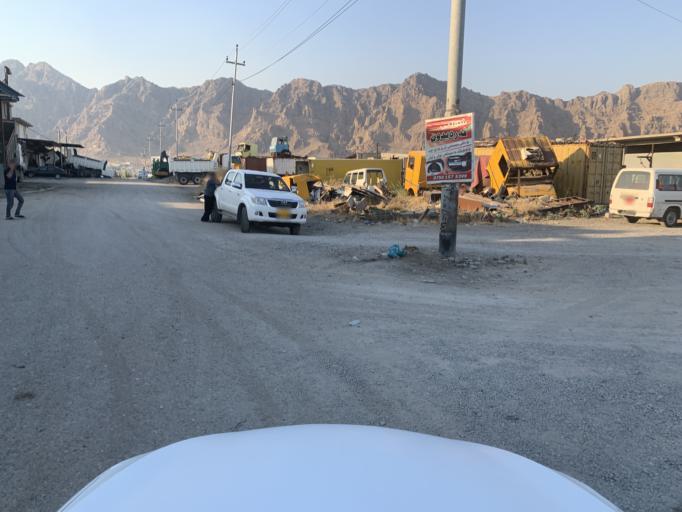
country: IQ
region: As Sulaymaniyah
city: Raniye
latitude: 36.2446
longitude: 44.8886
